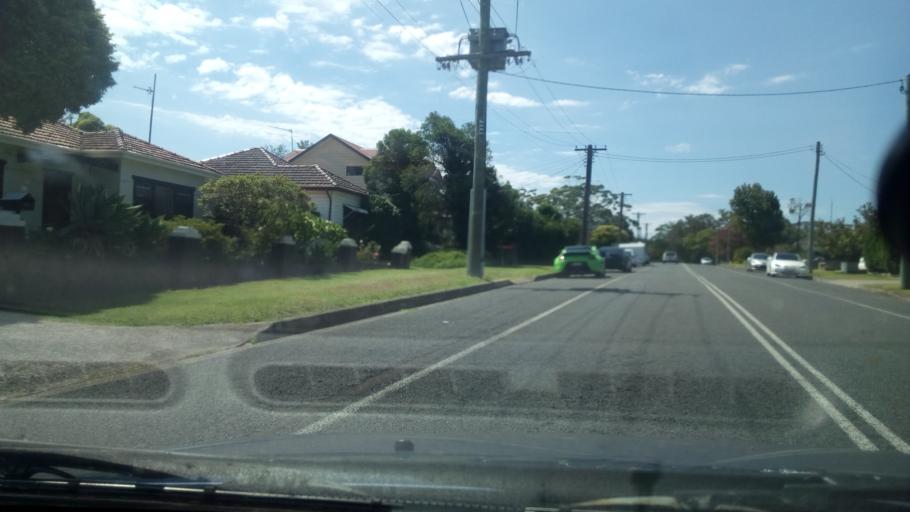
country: AU
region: New South Wales
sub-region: Wollongong
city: Keiraville
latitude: -34.4136
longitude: 150.8751
